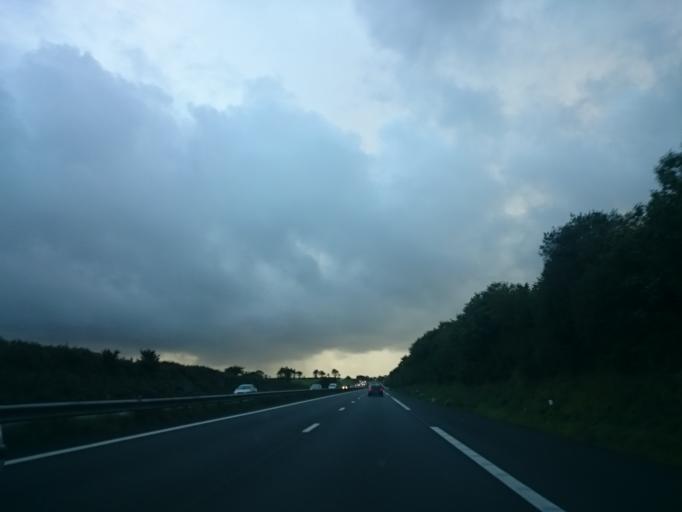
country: FR
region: Brittany
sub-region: Departement du Finistere
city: Saint-Thonan
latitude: 48.4803
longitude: -4.3047
